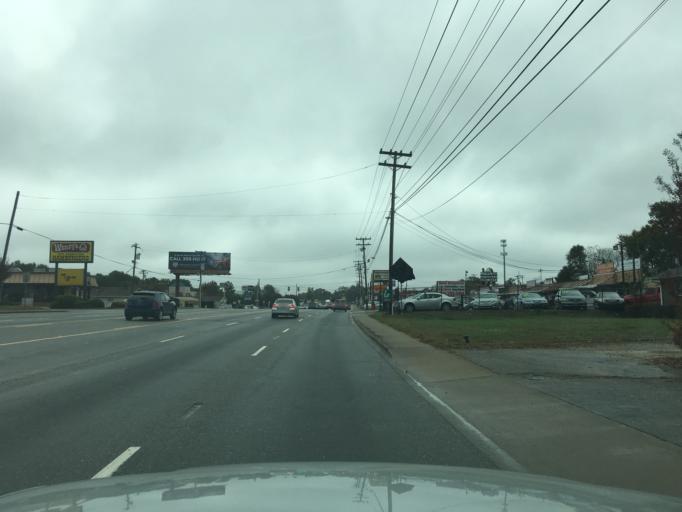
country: US
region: South Carolina
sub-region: Greenville County
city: Welcome
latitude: 34.8168
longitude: -82.4422
